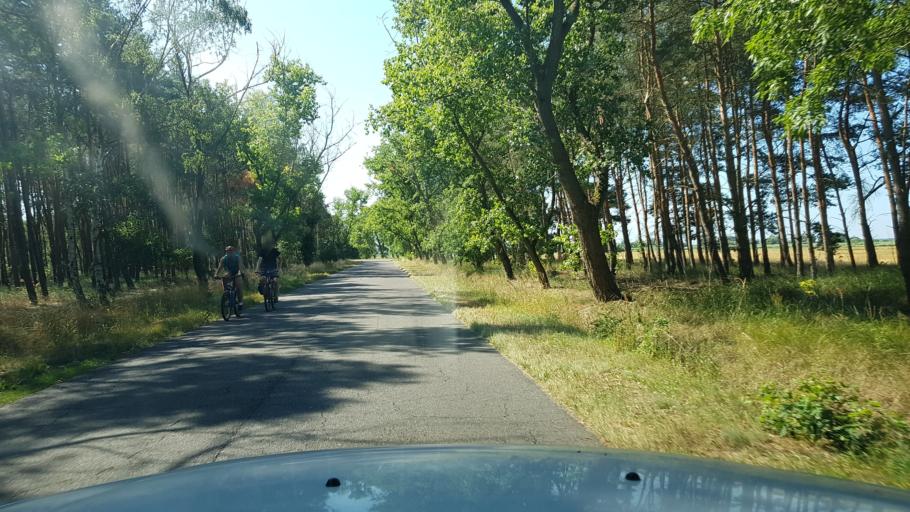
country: PL
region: West Pomeranian Voivodeship
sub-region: Powiat goleniowski
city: Goleniow
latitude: 53.4813
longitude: 14.7108
